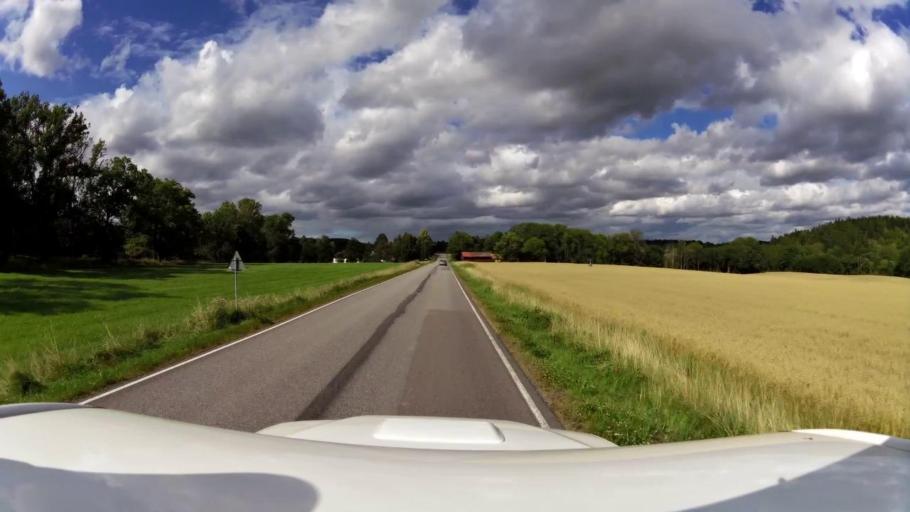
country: SE
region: OEstergoetland
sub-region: Linkopings Kommun
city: Sturefors
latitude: 58.3079
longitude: 15.7256
